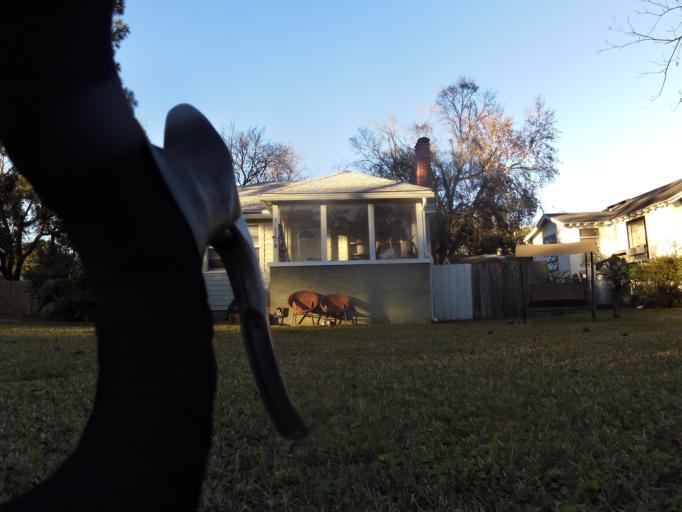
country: US
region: Florida
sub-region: Duval County
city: Jacksonville
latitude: 30.3176
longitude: -81.7079
